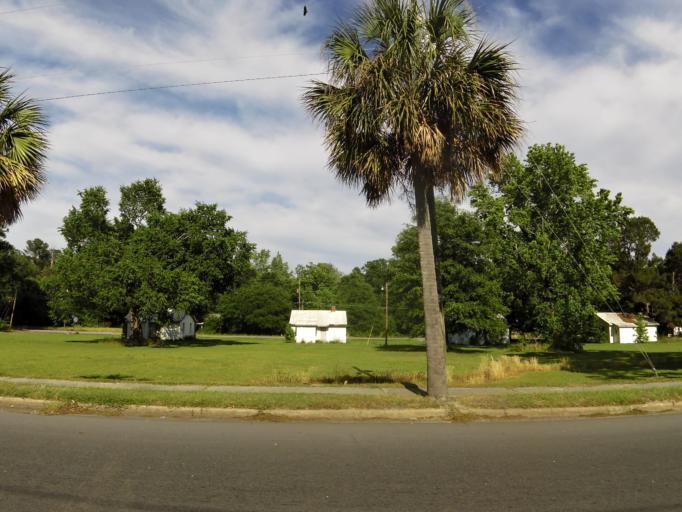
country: US
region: South Carolina
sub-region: Allendale County
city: Fairfax
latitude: 32.9537
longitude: -81.2359
